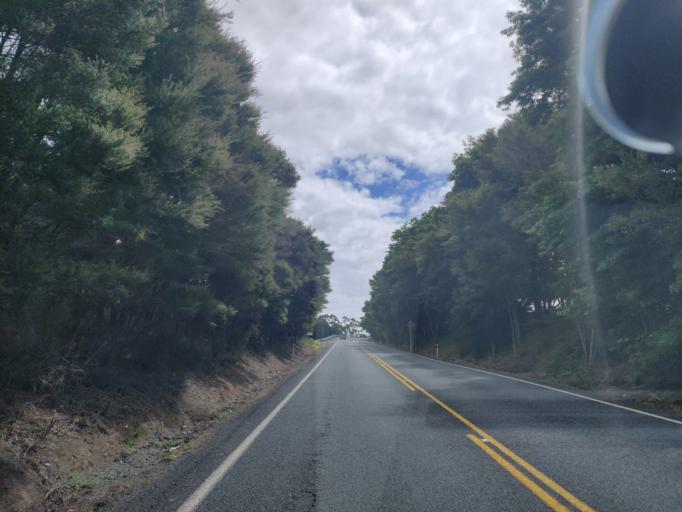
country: NZ
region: Northland
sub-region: Far North District
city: Paihia
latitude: -35.2910
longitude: 174.0119
